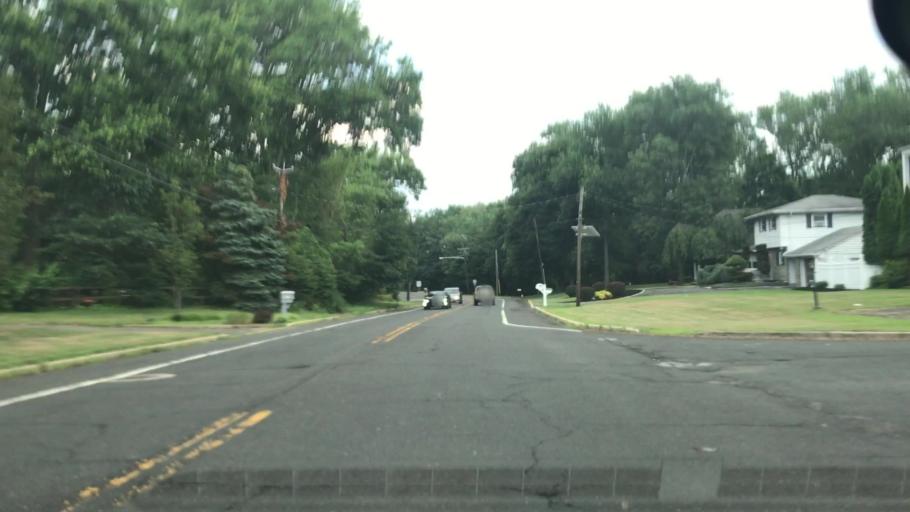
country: US
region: New Jersey
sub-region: Somerset County
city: Bradley Gardens
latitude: 40.5555
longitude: -74.6747
